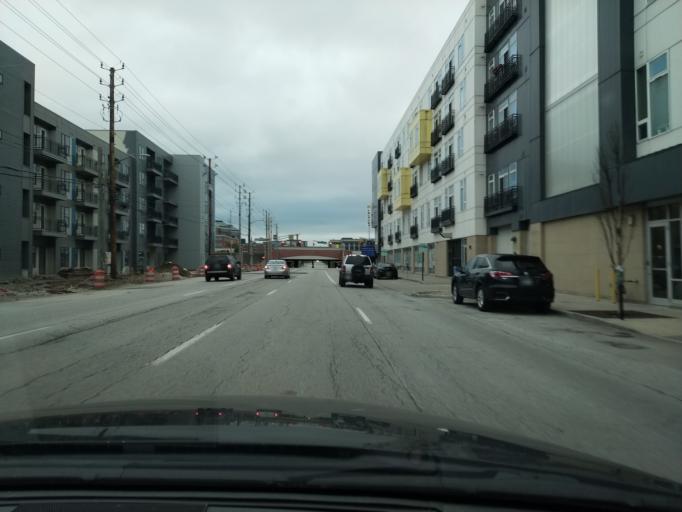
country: US
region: Indiana
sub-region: Marion County
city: Indianapolis
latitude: 39.7678
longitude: -86.1491
